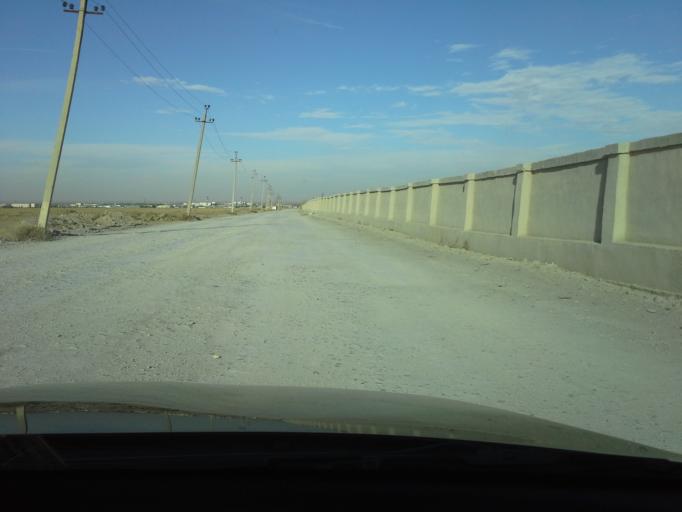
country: TM
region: Ahal
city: Abadan
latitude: 38.0331
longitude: 58.1597
